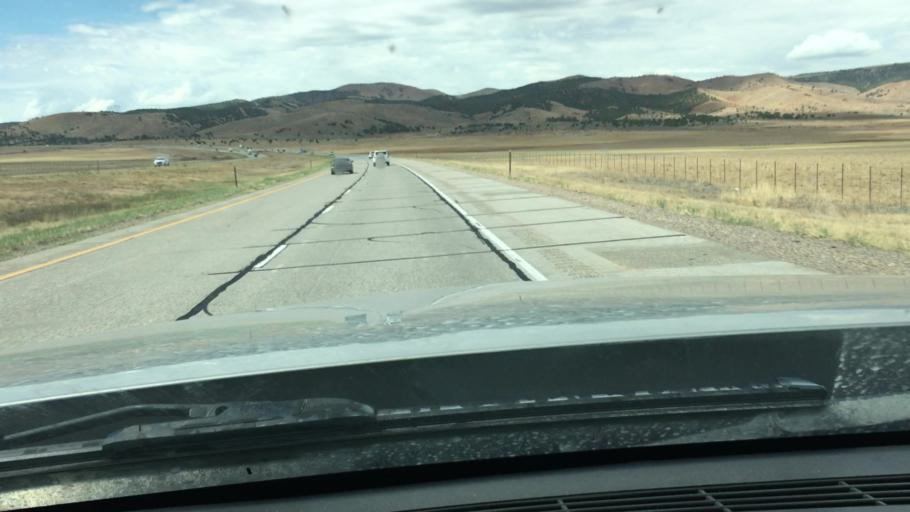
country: US
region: Utah
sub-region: Juab County
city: Nephi
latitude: 39.6582
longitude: -111.8864
